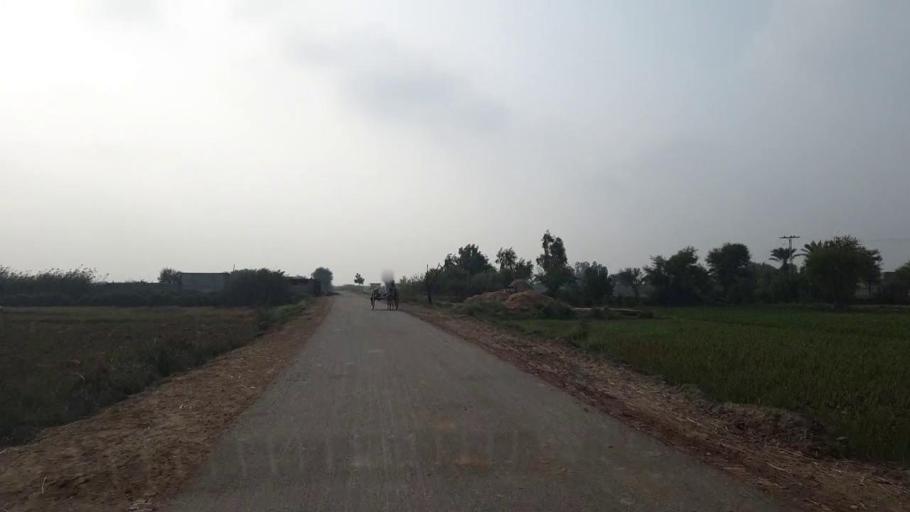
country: PK
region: Sindh
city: Tando Muhammad Khan
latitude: 25.1325
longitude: 68.5951
